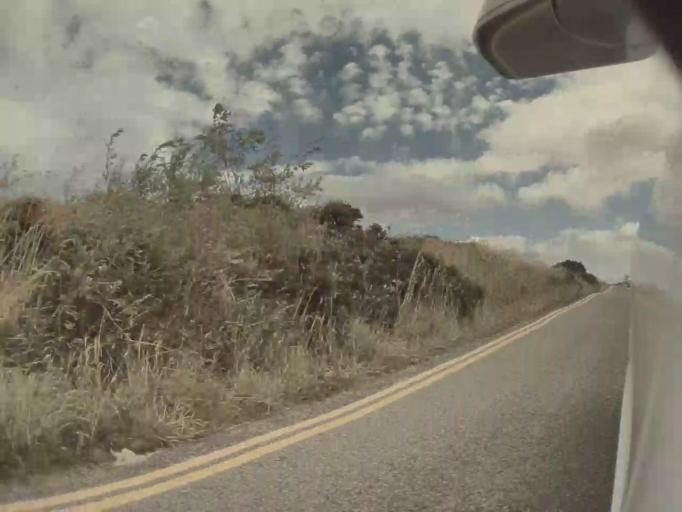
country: IE
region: Leinster
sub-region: Wicklow
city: Kilmacanoge
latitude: 53.1449
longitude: -6.1595
